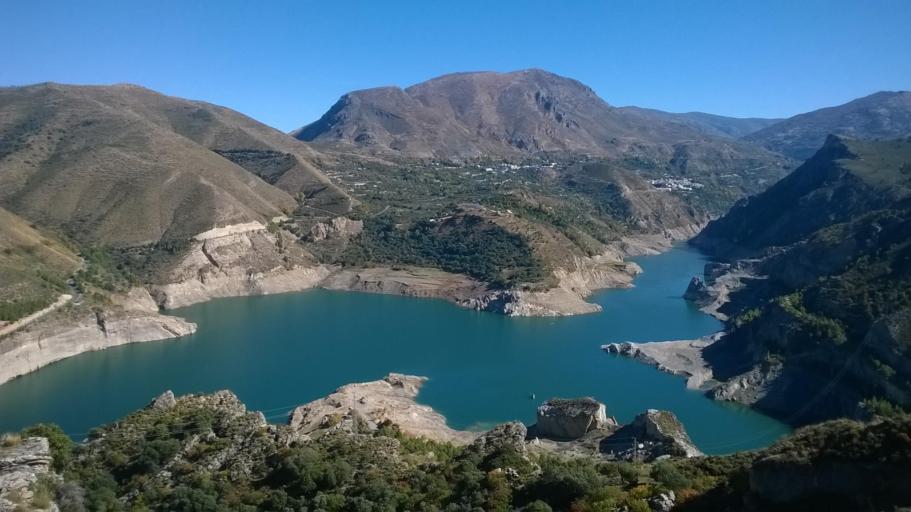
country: ES
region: Andalusia
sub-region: Provincia de Granada
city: Pinos Genil
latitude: 37.1522
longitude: -3.4784
